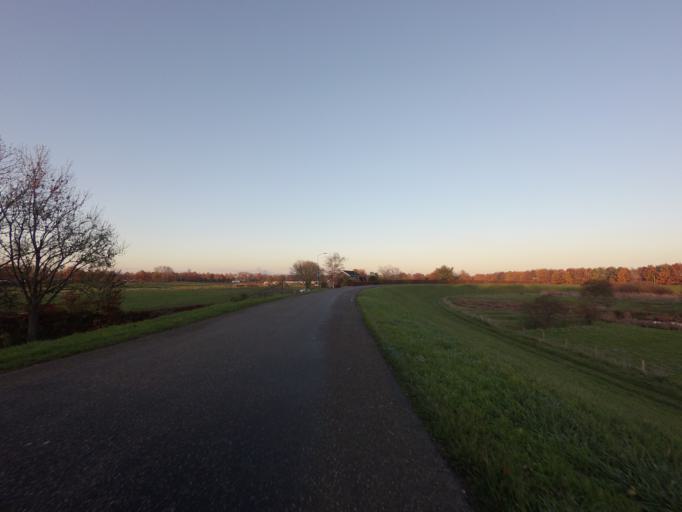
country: NL
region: Gelderland
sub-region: Gemeente Zaltbommel
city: Nederhemert-Noord
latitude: 51.7470
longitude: 5.2080
